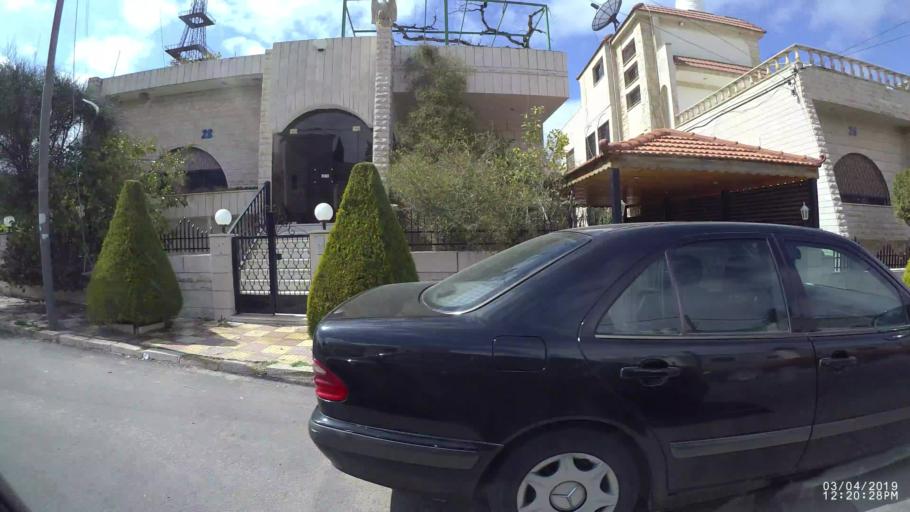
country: JO
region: Amman
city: Wadi as Sir
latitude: 31.9675
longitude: 35.8391
